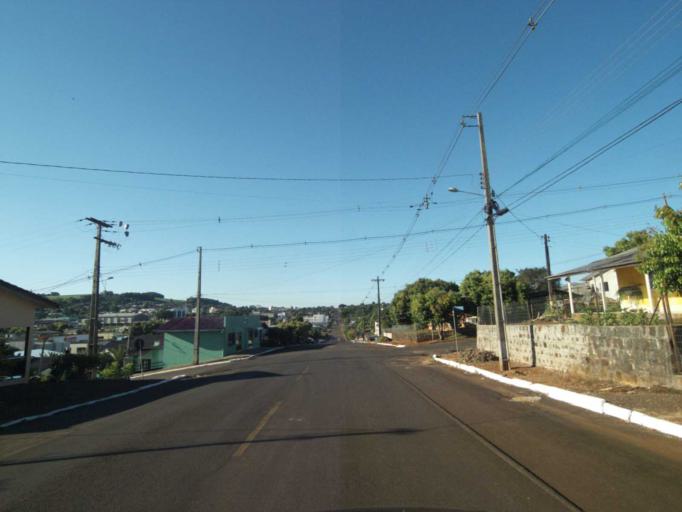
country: BR
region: Parana
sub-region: Coronel Vivida
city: Coronel Vivida
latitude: -25.9692
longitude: -52.8132
